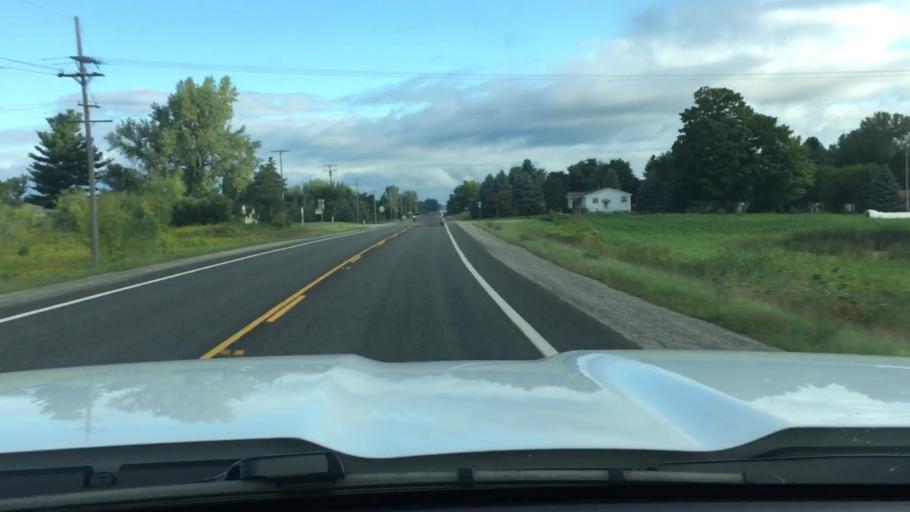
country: US
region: Michigan
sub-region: Tuscola County
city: Caro
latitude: 43.3498
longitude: -83.3826
